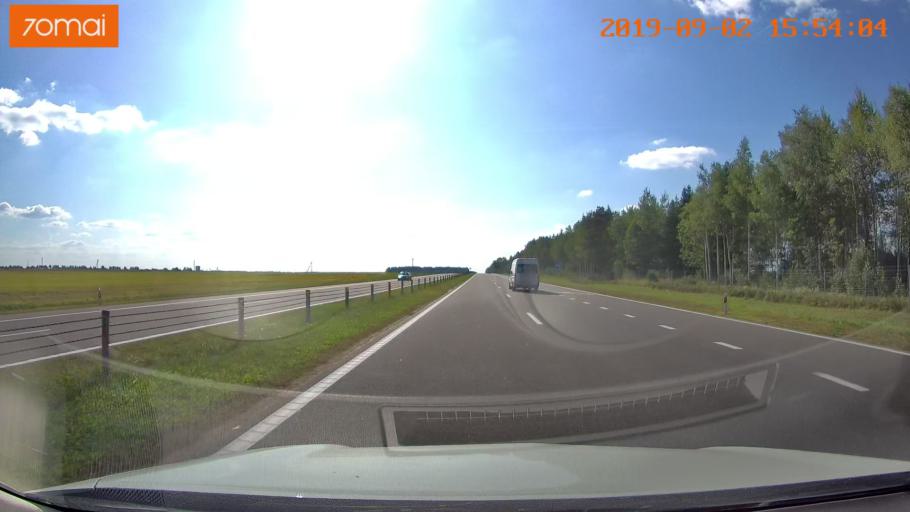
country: BY
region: Minsk
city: Byerazino
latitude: 53.8559
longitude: 29.1353
